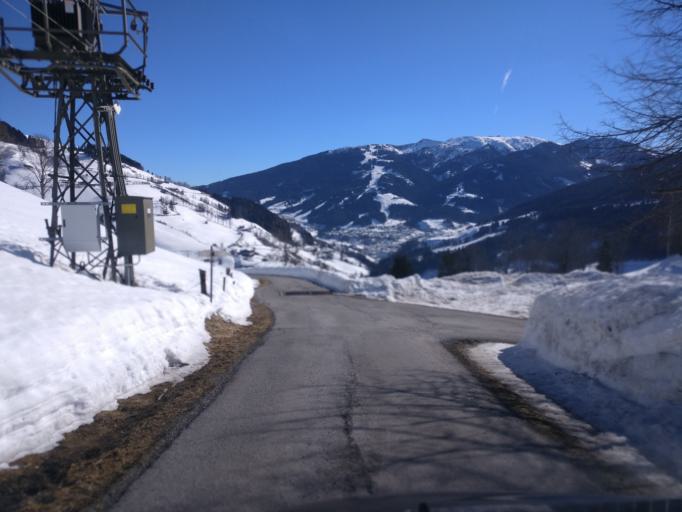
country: AT
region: Salzburg
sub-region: Politischer Bezirk Sankt Johann im Pongau
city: Wagrain
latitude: 47.3406
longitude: 13.2559
